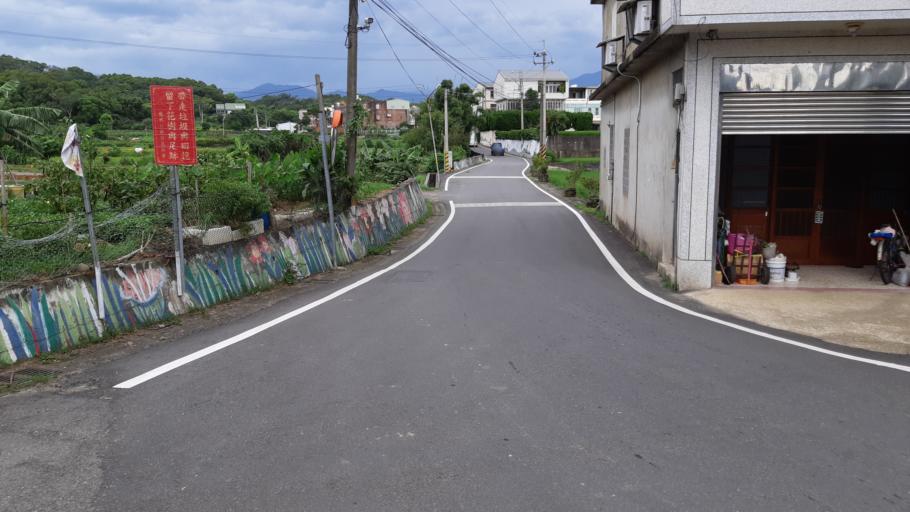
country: TW
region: Taiwan
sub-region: Miaoli
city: Miaoli
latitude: 24.6585
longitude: 120.8867
